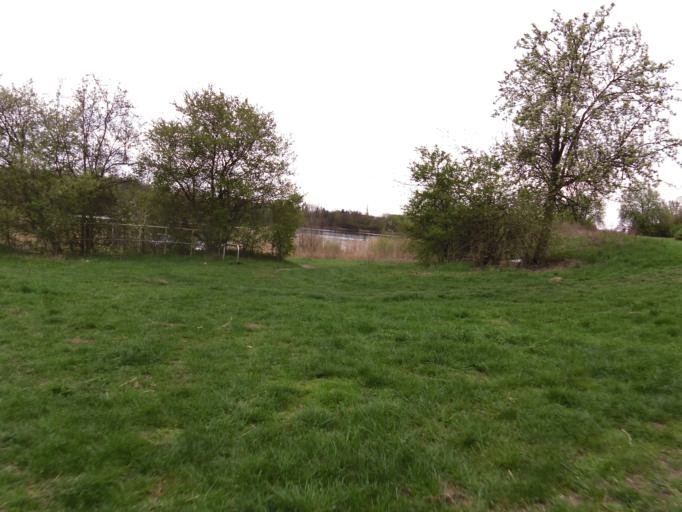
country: DE
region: Saxony
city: Markkleeberg
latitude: 51.2924
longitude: 12.3161
